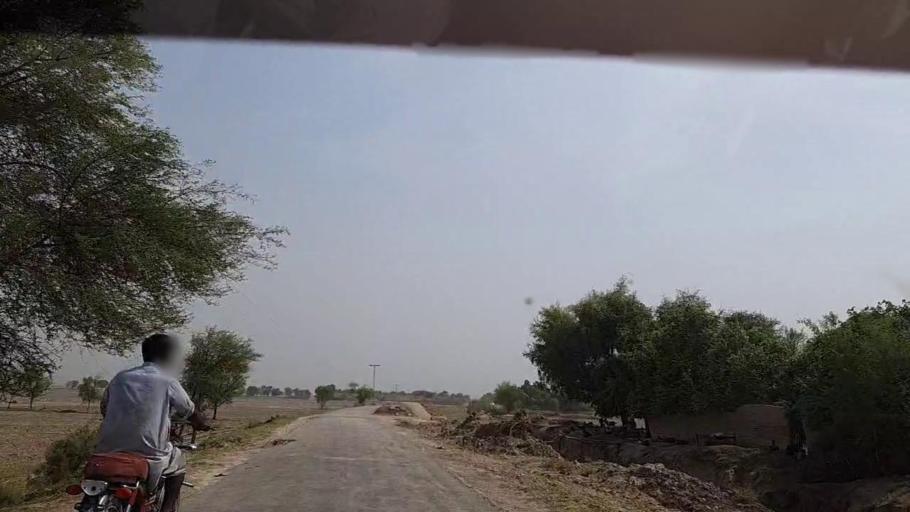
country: PK
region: Sindh
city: Khairpur Nathan Shah
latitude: 27.0706
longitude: 67.6880
